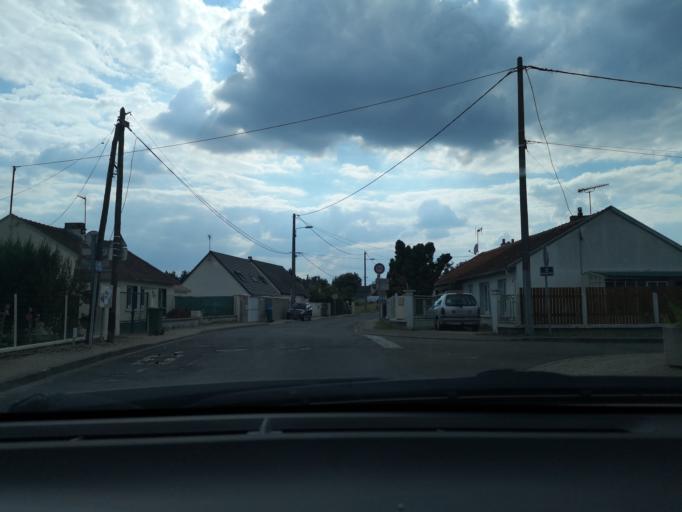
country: FR
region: Centre
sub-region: Departement du Loiret
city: Semoy
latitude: 47.9273
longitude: 1.9441
